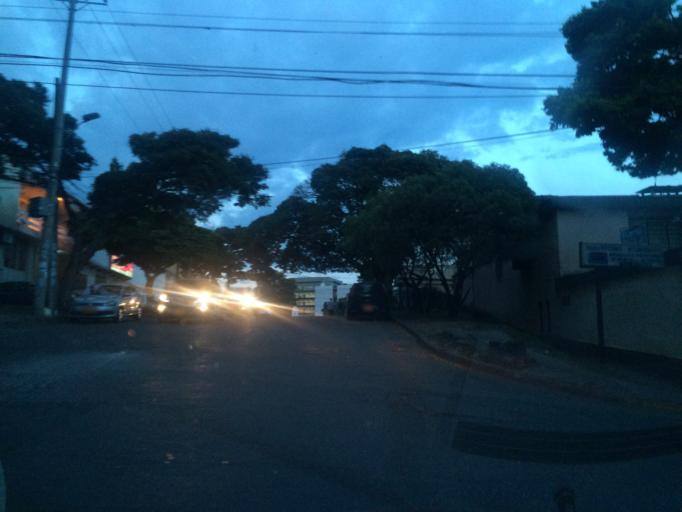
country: CO
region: Valle del Cauca
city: Cali
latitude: 3.4265
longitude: -76.5485
